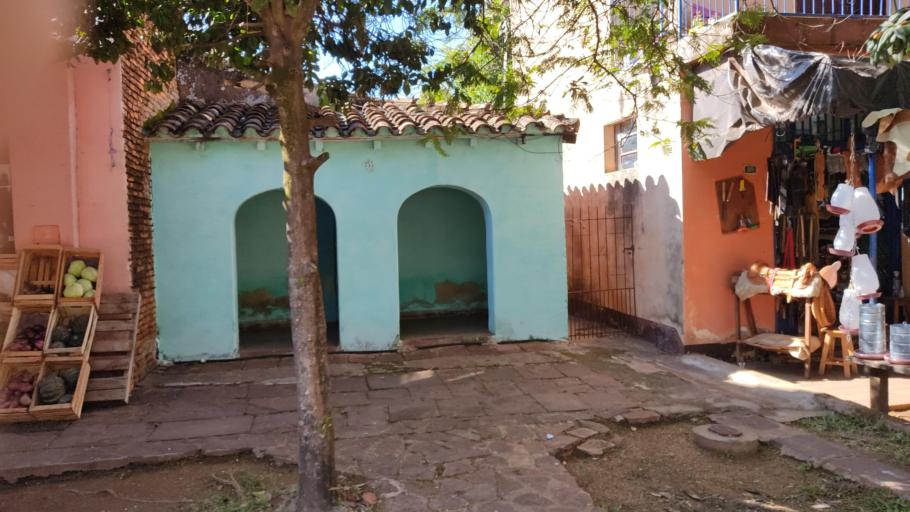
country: PY
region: Misiones
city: San Juan Bautista
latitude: -26.6702
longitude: -57.1393
